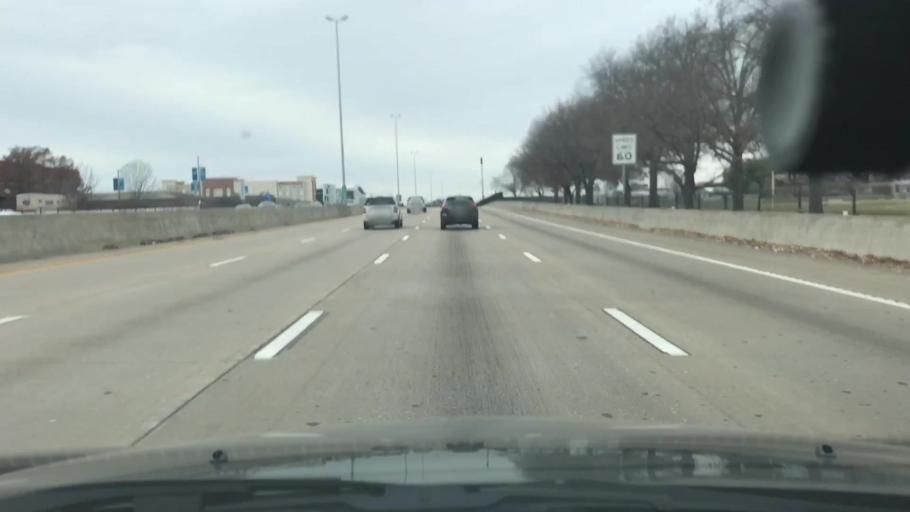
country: US
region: Missouri
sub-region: Saint Louis County
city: University City
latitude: 38.6303
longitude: -90.2764
